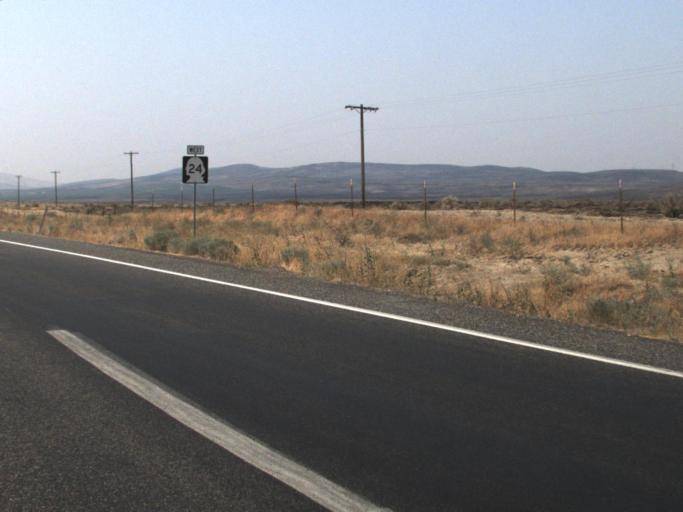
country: US
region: Washington
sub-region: Grant County
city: Desert Aire
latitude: 46.5773
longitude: -119.7295
